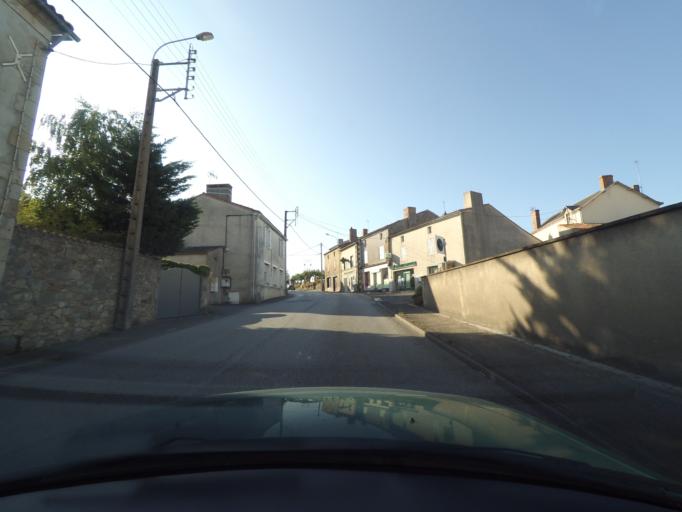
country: FR
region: Poitou-Charentes
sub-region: Departement des Deux-Sevres
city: Chiche
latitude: 46.7974
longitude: -0.3600
